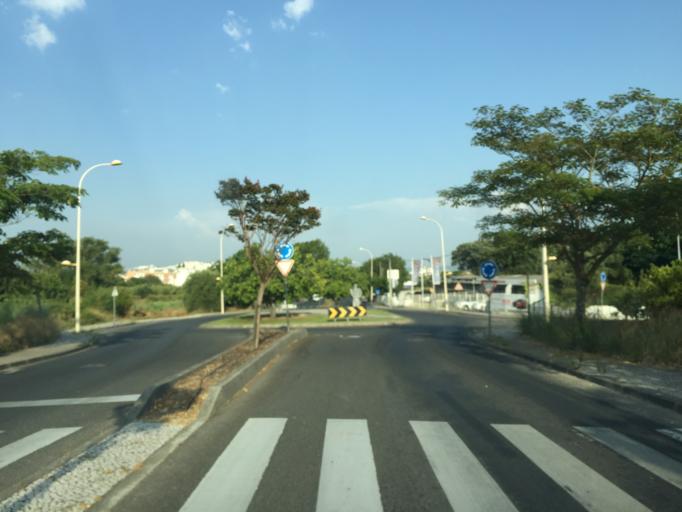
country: PT
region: Santarem
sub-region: Torres Novas
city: Torres Novas
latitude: 39.4738
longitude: -8.5533
